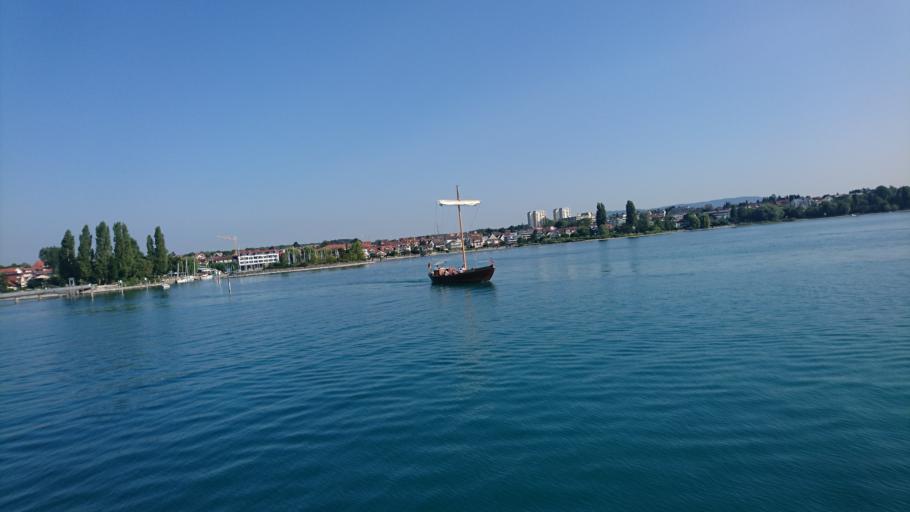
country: DE
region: Baden-Wuerttemberg
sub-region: Tuebingen Region
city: Immenstaad am Bodensee
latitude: 47.6599
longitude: 9.3695
